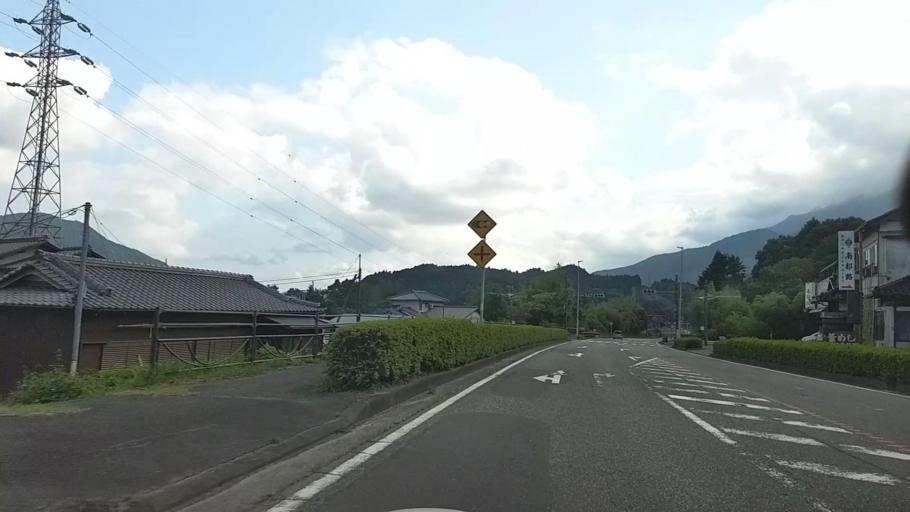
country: JP
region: Shizuoka
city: Fujinomiya
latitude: 35.3011
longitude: 138.4475
